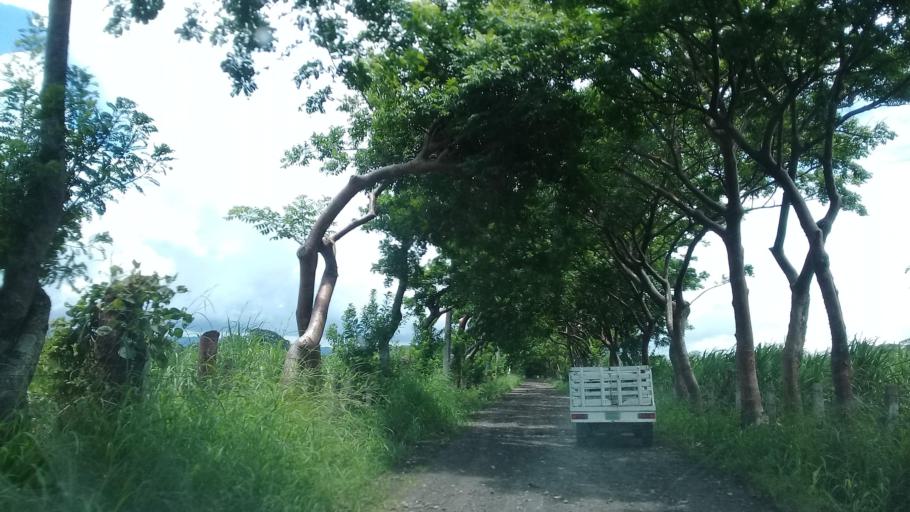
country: MX
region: Veracruz
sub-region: Naolinco
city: El Espinal
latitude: 19.5884
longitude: -96.8621
